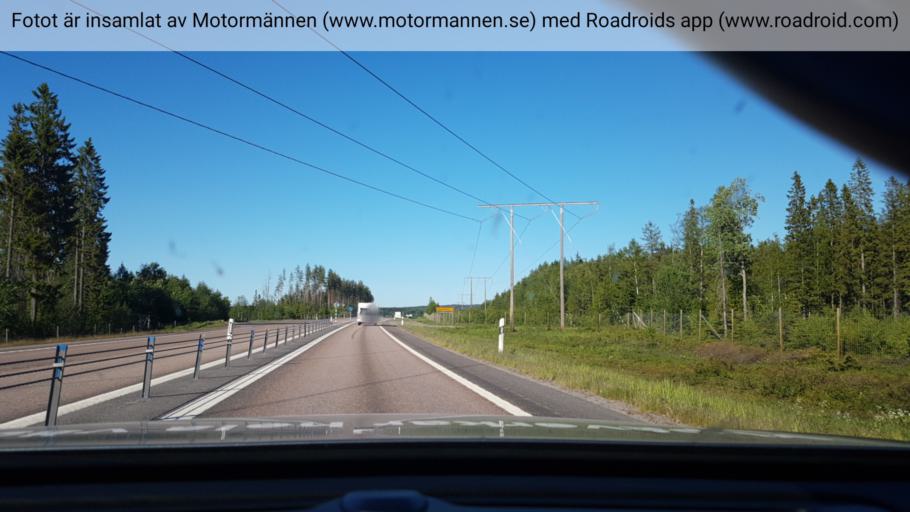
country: SE
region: Vaesternorrland
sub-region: Haernoesands Kommun
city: Haernoesand
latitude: 62.5748
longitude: 17.7490
